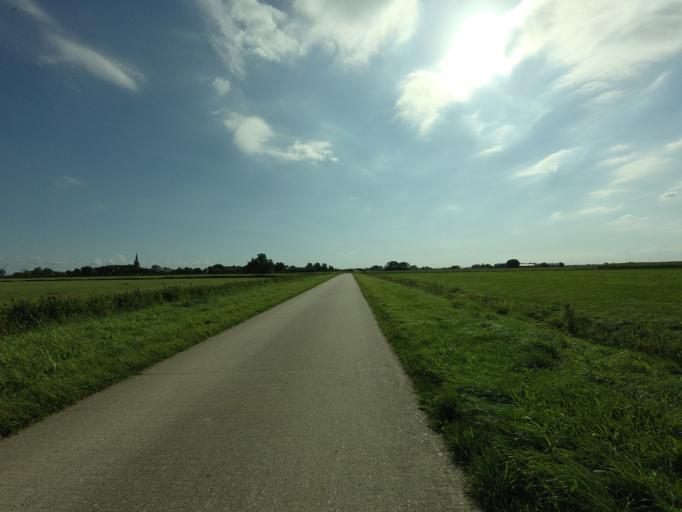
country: NL
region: Friesland
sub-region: Gemeente Littenseradiel
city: Makkum
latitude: 53.0808
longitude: 5.6317
